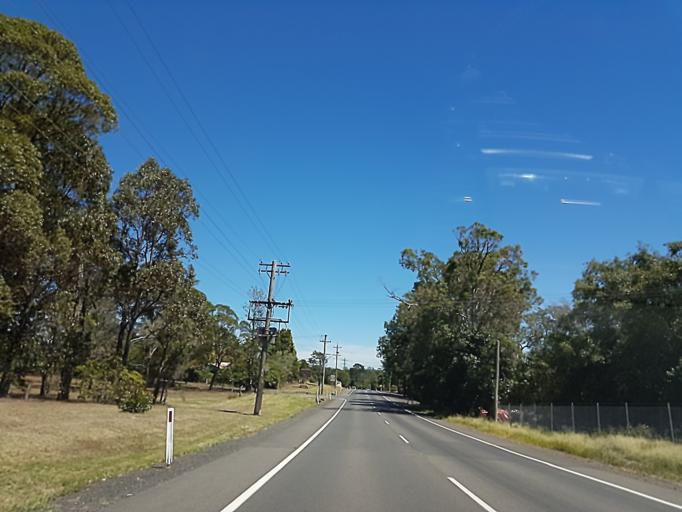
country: AU
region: New South Wales
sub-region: Hornsby Shire
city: Glenorie
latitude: -33.6074
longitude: 151.0164
